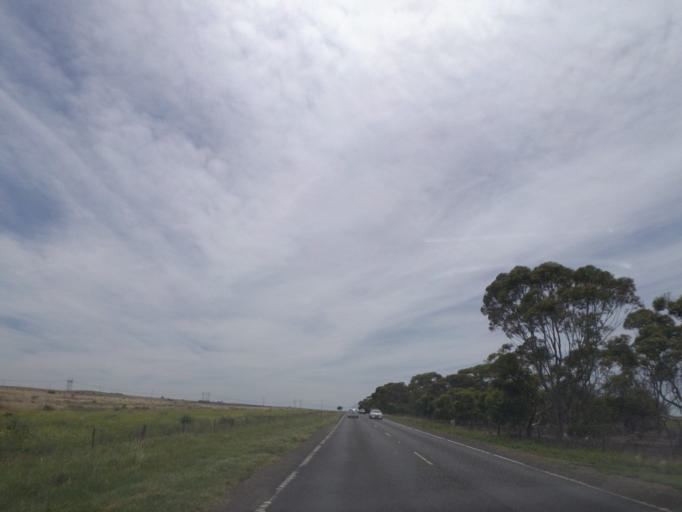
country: AU
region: Victoria
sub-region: Melton
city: Caroline Springs
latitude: -37.7817
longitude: 144.6995
